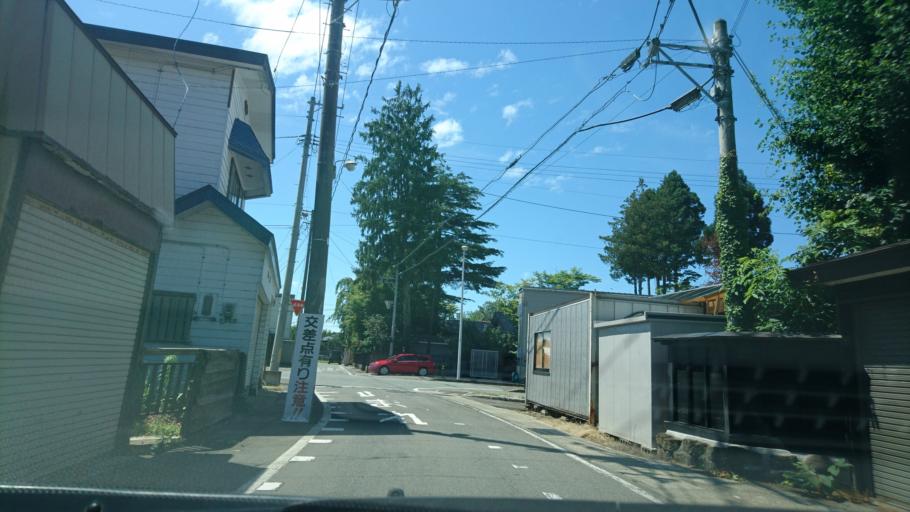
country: JP
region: Akita
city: Kakunodatemachi
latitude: 39.5847
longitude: 140.5635
